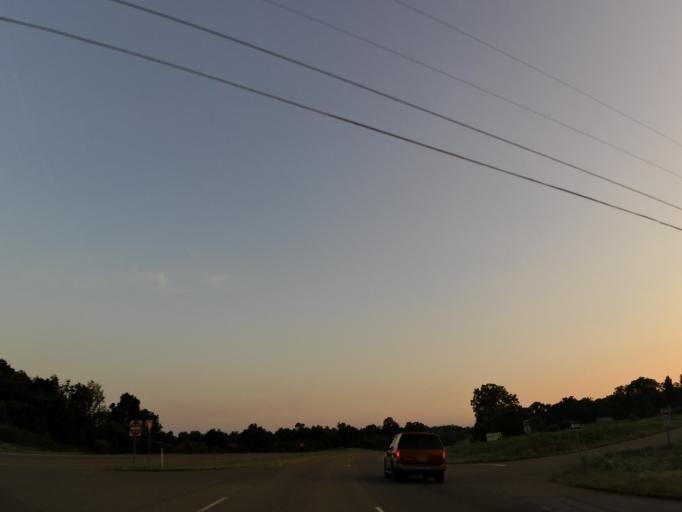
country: US
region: Tennessee
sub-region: Carroll County
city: McKenzie
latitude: 36.1991
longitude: -88.4090
